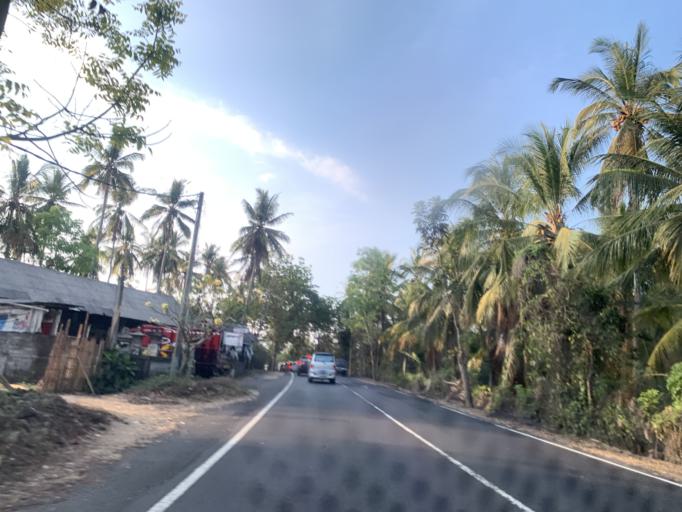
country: ID
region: Bali
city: Angkahgede
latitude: -8.4864
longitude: 114.9500
